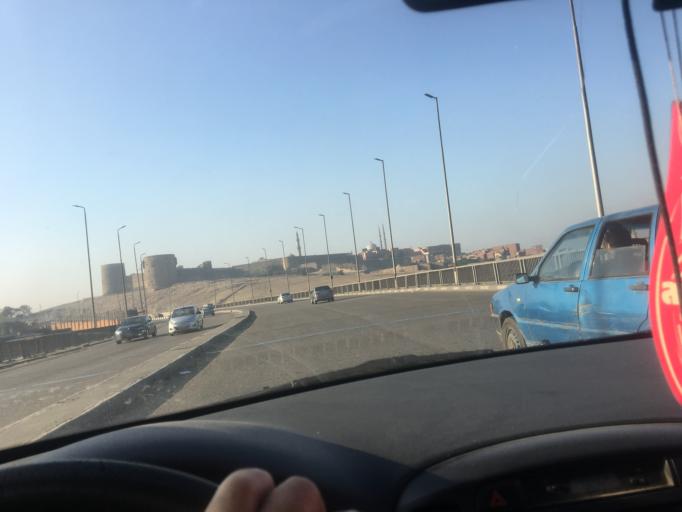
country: EG
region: Muhafazat al Qahirah
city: Cairo
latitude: 30.0348
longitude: 31.2683
